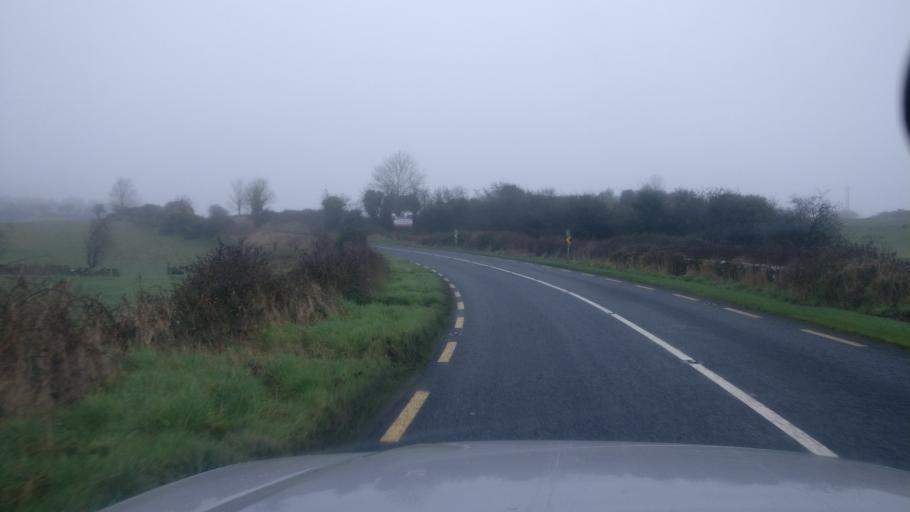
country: IE
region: Connaught
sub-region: County Galway
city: Loughrea
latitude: 53.1872
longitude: -8.6094
